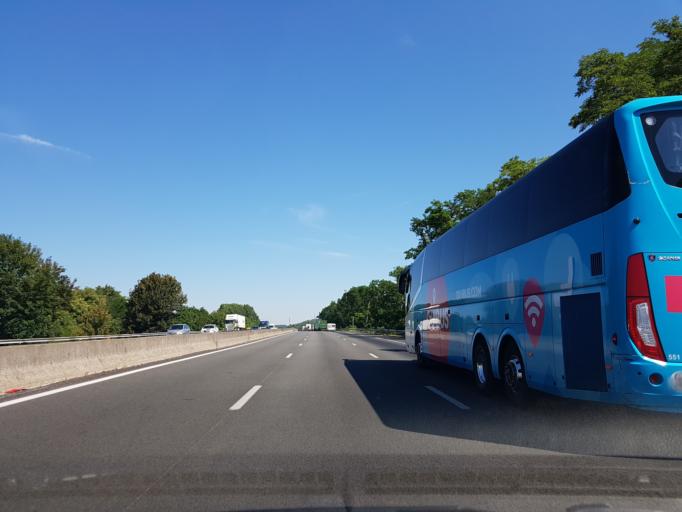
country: FR
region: Picardie
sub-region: Departement de l'Oise
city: Longueil-Sainte-Marie
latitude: 49.3802
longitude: 2.7034
